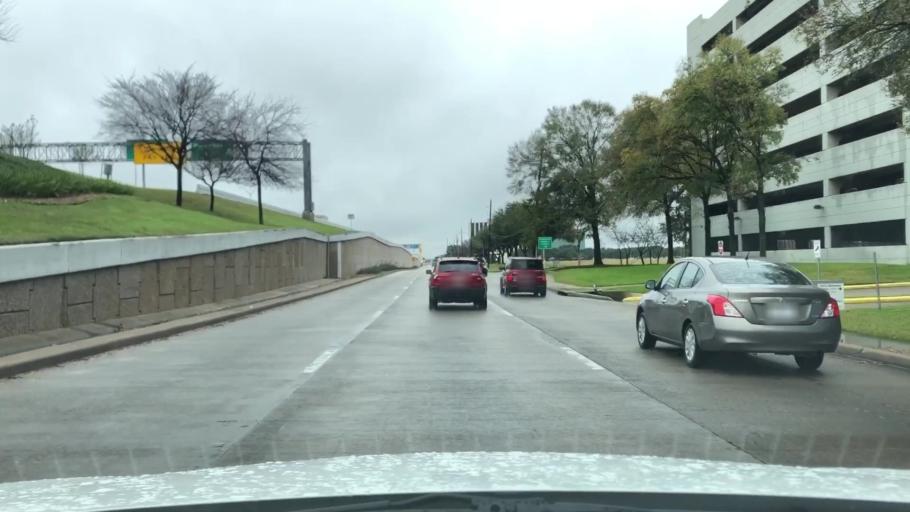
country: US
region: Texas
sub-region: Harris County
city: Bunker Hill Village
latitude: 29.7281
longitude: -95.5569
